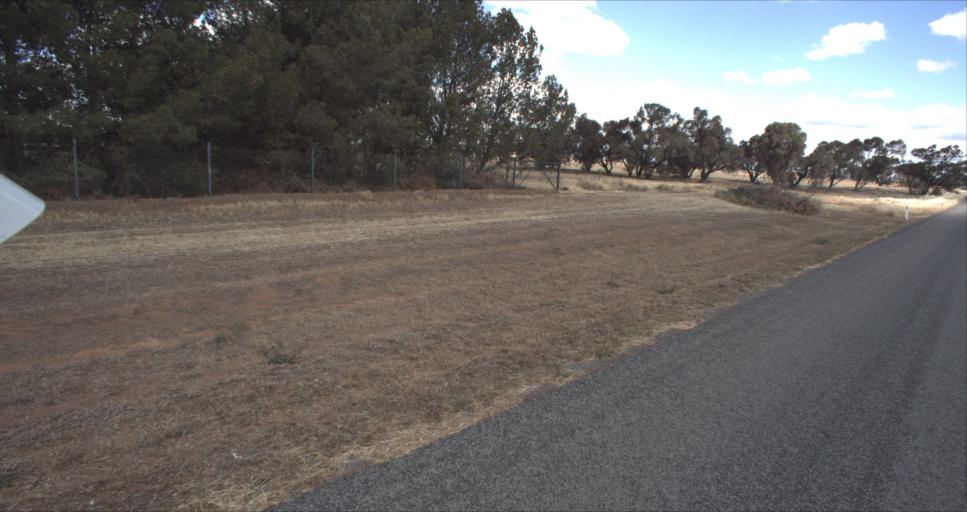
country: AU
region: New South Wales
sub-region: Leeton
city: Leeton
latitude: -34.4853
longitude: 146.2483
